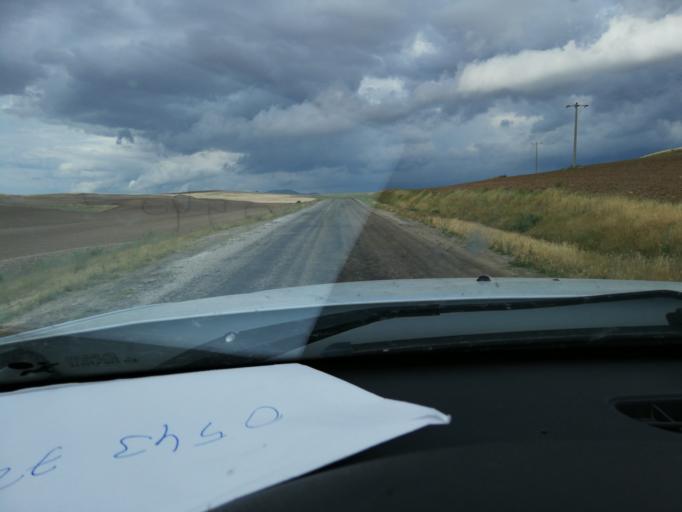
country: TR
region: Kirsehir
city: Kirsehir
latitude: 39.0415
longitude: 34.1539
